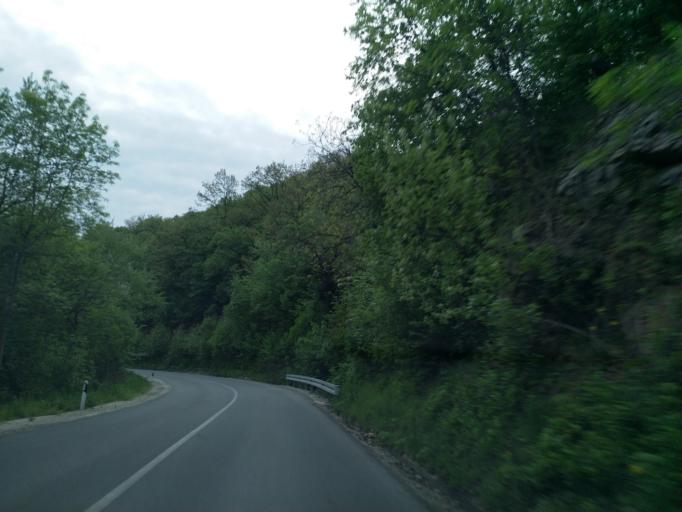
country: RS
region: Central Serbia
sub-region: Pomoravski Okrug
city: Despotovac
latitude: 43.9753
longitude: 21.5108
